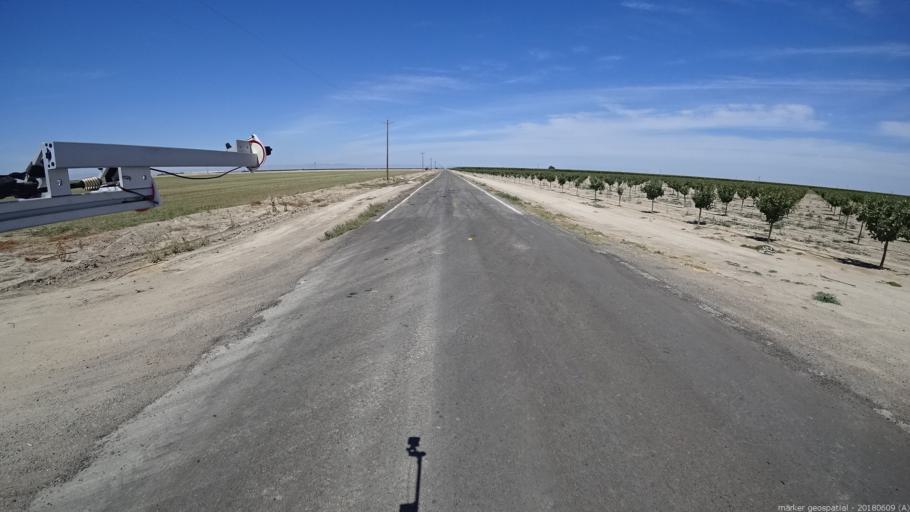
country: US
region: California
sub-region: Fresno County
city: Firebaugh
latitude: 36.9526
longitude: -120.3596
